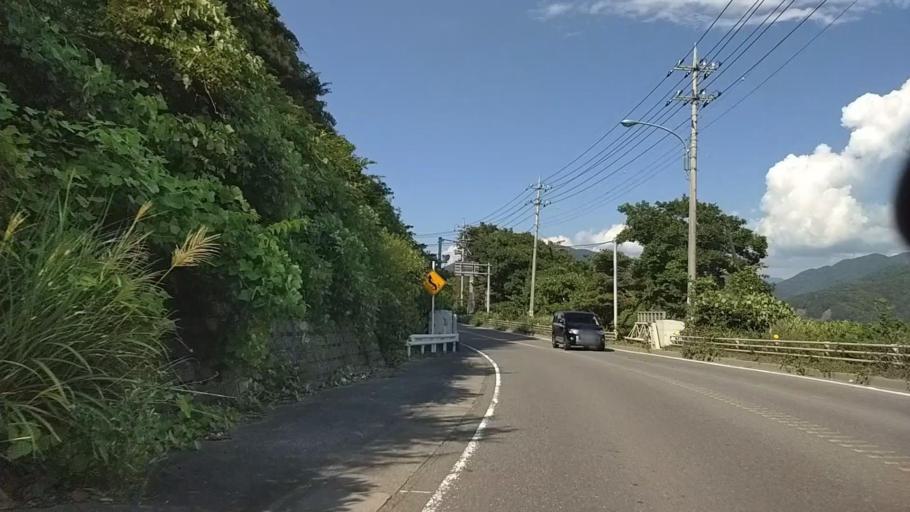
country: JP
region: Shizuoka
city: Fujinomiya
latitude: 35.3997
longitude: 138.4427
